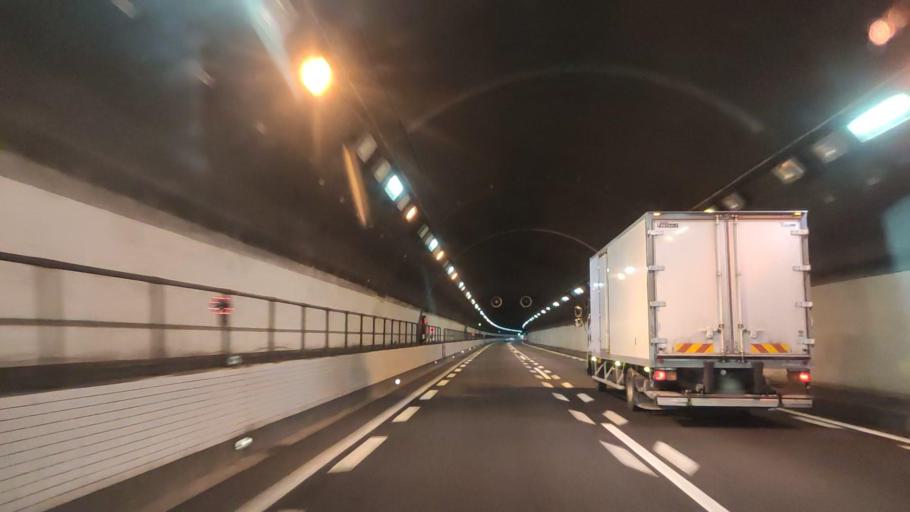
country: JP
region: Hiroshima
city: Fukuyama
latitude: 34.5091
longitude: 133.3346
